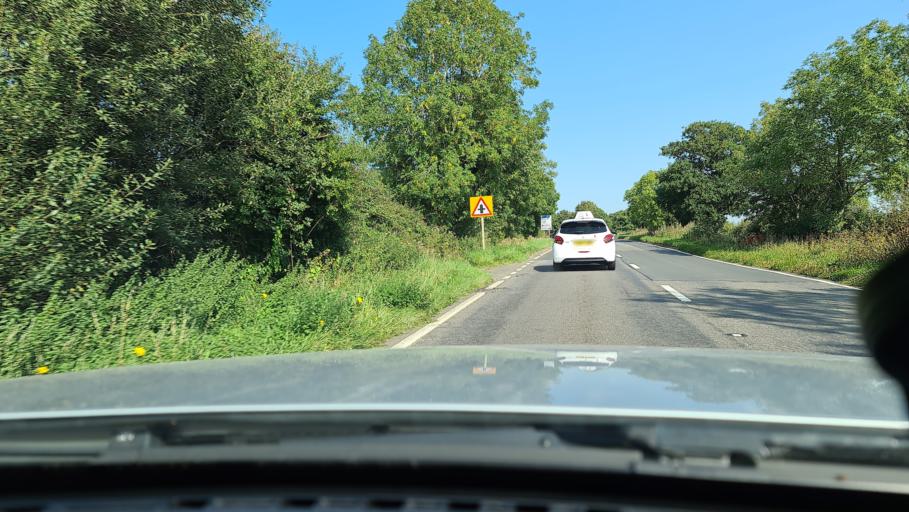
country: GB
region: England
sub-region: Northamptonshire
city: Daventry
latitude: 52.2939
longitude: -1.1674
